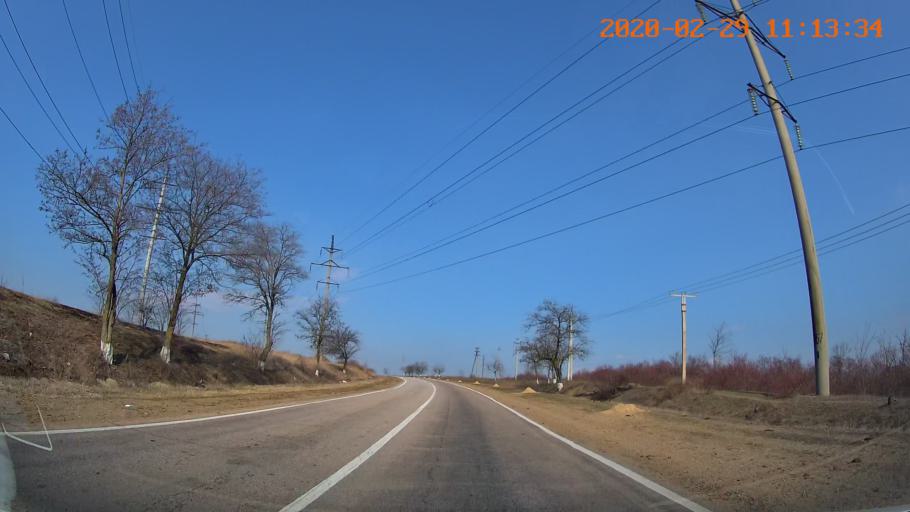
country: MD
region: Telenesti
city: Dubasari
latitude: 47.2734
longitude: 29.1808
